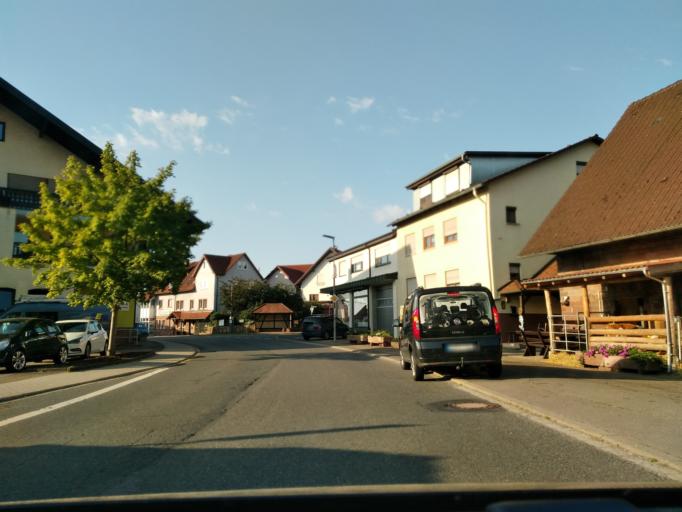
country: DE
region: Baden-Wuerttemberg
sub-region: Karlsruhe Region
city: Fahrenbach
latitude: 49.4308
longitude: 9.1498
